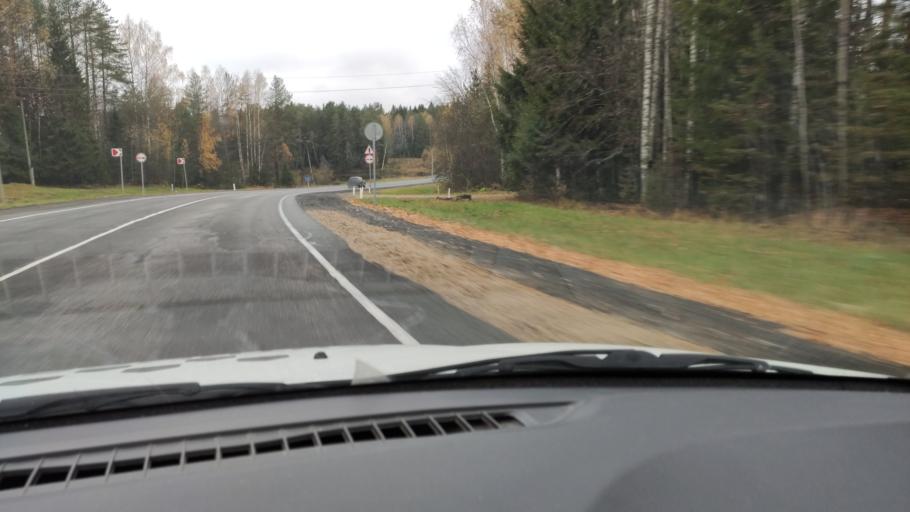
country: RU
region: Kirov
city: Belaya Kholunitsa
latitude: 58.9043
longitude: 50.9485
